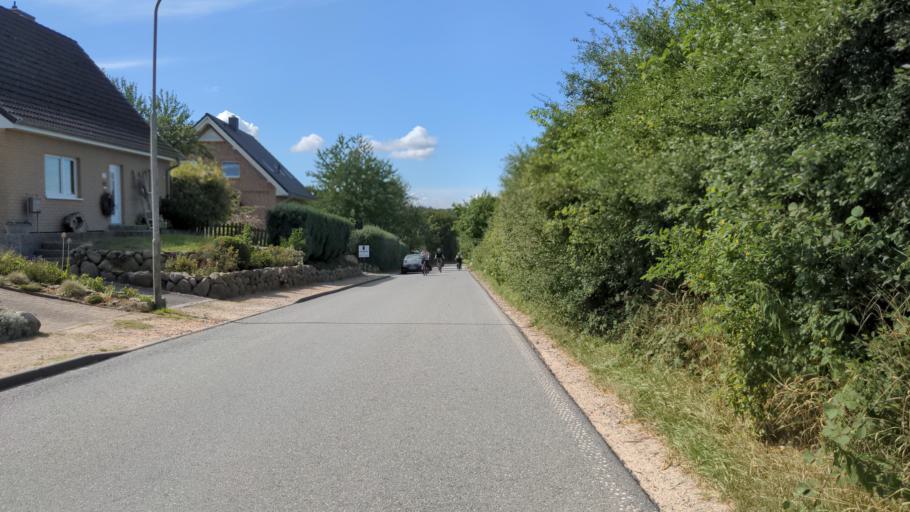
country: DE
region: Schleswig-Holstein
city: Malente
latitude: 54.1823
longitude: 10.5376
